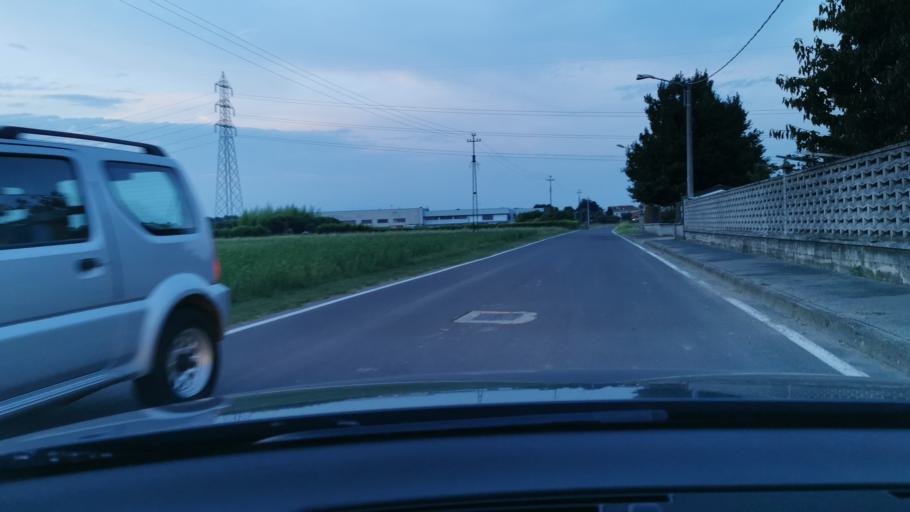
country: IT
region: Lombardy
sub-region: Provincia di Varese
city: Gerenzano
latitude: 45.6409
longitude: 8.9869
